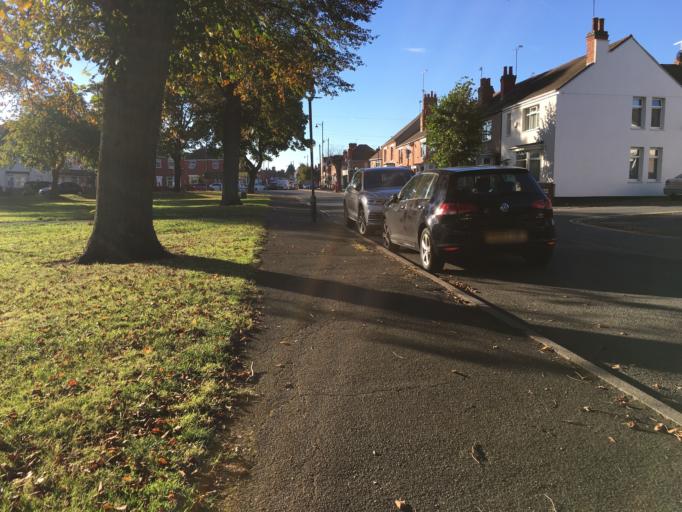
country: GB
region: England
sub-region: Warwickshire
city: Nuneaton
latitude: 52.5268
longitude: -1.4715
